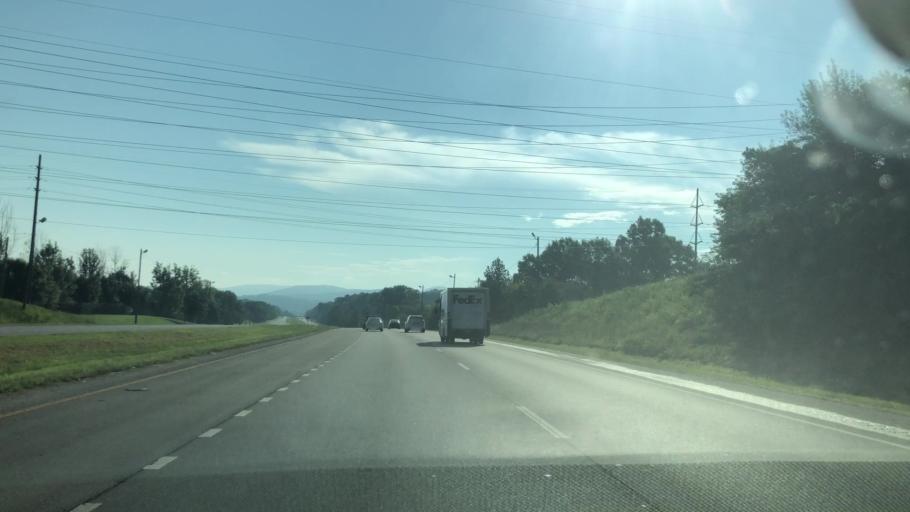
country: US
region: Alabama
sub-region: Calhoun County
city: West End-Cobb Town
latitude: 33.6479
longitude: -85.8574
